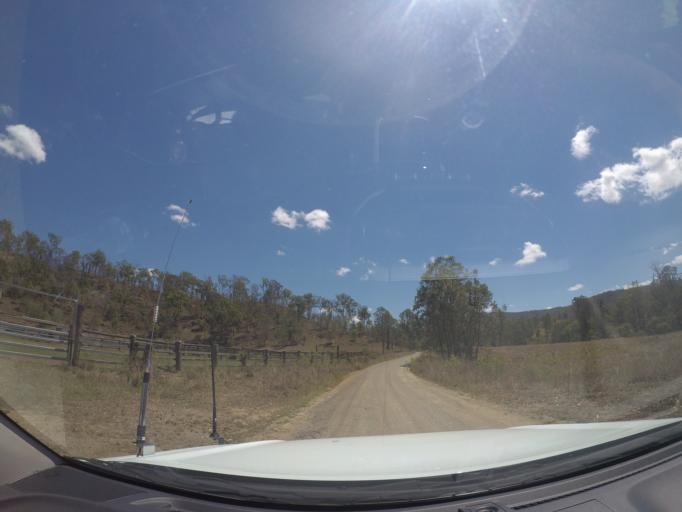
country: AU
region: Queensland
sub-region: Ipswich
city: Springfield Lakes
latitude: -27.8209
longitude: 152.8577
